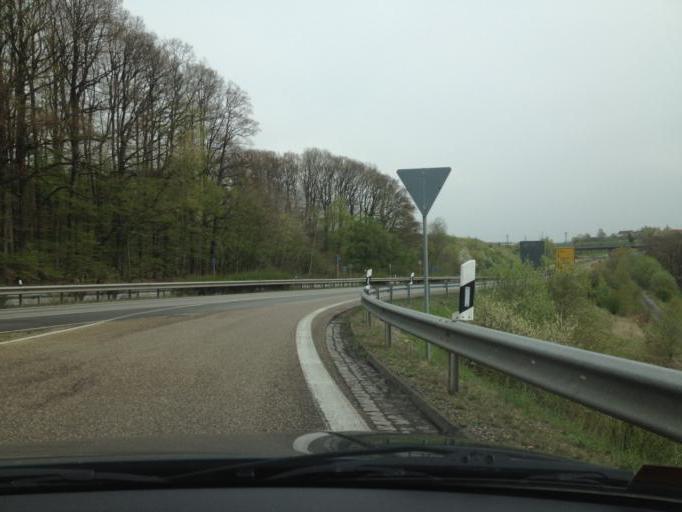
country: DE
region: Rheinland-Pfalz
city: Petersberg
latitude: 49.2314
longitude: 7.5606
